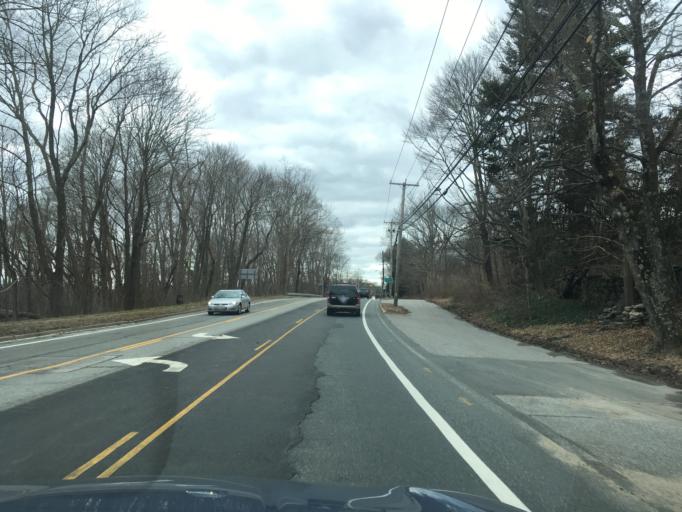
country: US
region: Rhode Island
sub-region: Washington County
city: North Kingstown
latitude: 41.5790
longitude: -71.4599
